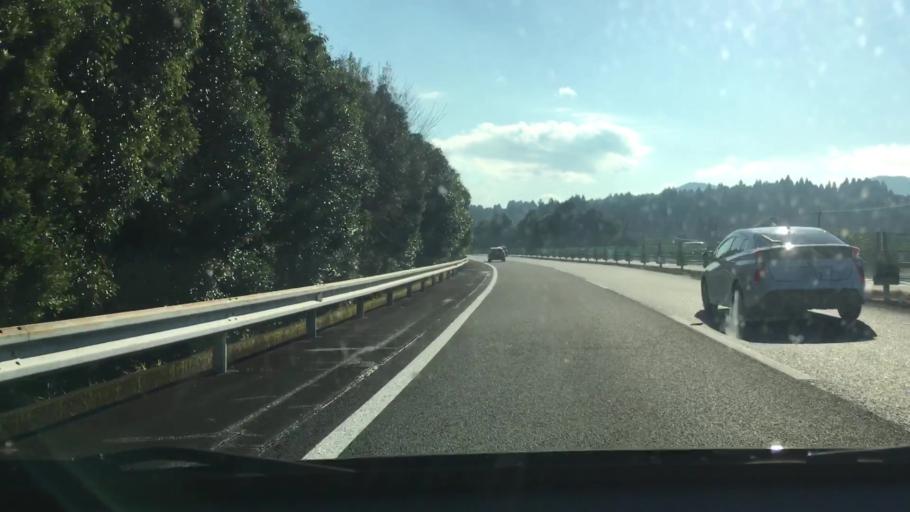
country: JP
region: Kagoshima
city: Okuchi-shinohara
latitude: 32.0108
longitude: 130.7569
